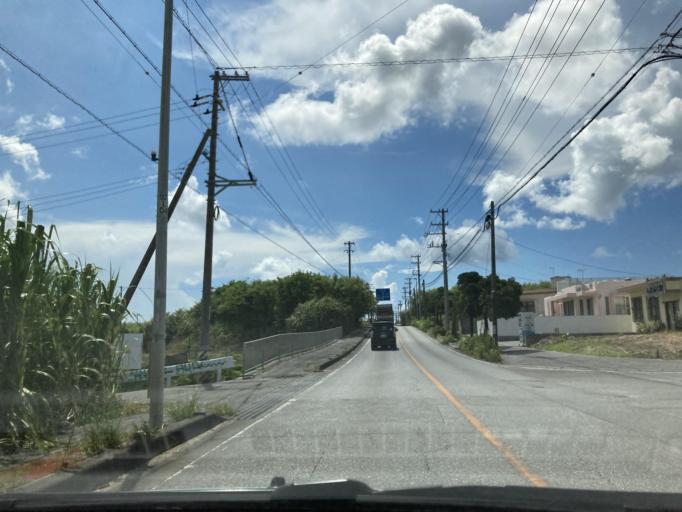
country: JP
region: Okinawa
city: Itoman
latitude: 26.1370
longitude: 127.7299
